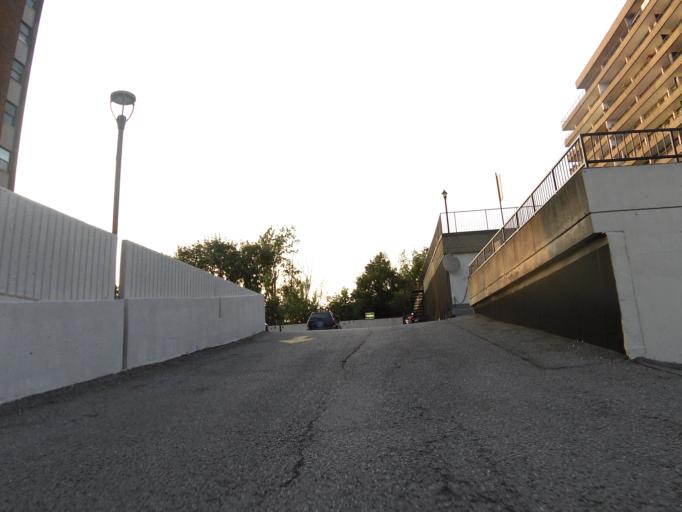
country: CA
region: Ontario
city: Ottawa
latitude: 45.3909
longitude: -75.7599
